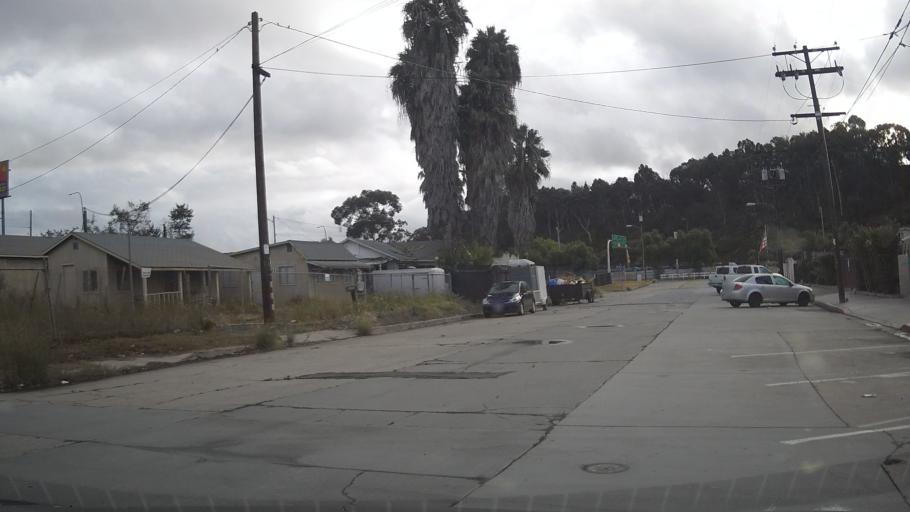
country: US
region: California
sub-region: San Diego County
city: San Diego
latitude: 32.7144
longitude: -117.1200
